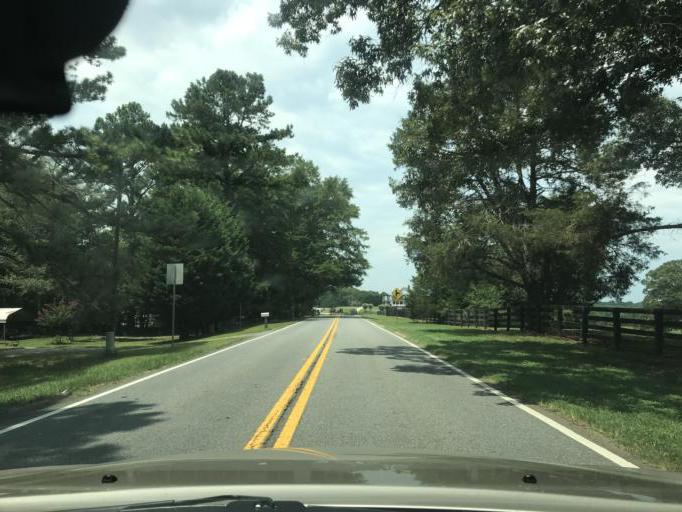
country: US
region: Georgia
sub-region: Forsyth County
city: Cumming
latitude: 34.2785
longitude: -84.2135
